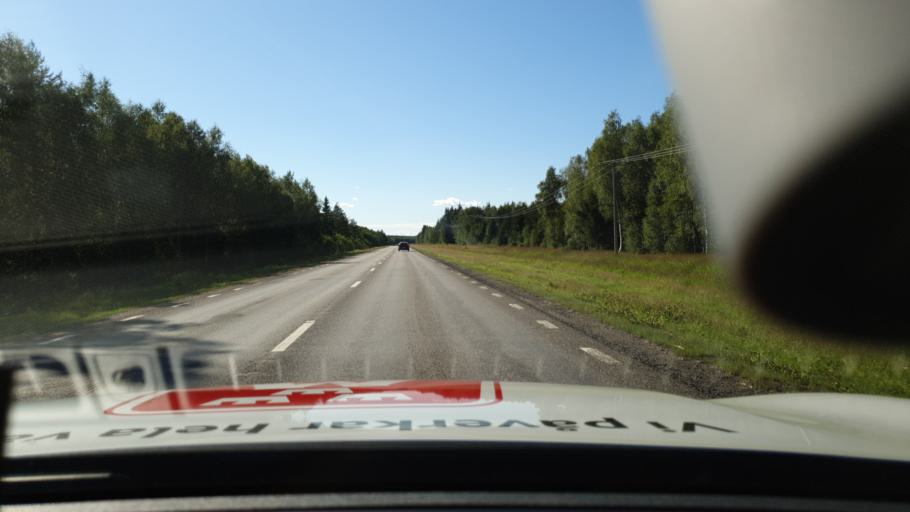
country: SE
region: Norrbotten
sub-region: Pitea Kommun
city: Rosvik
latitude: 65.5759
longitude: 21.7287
